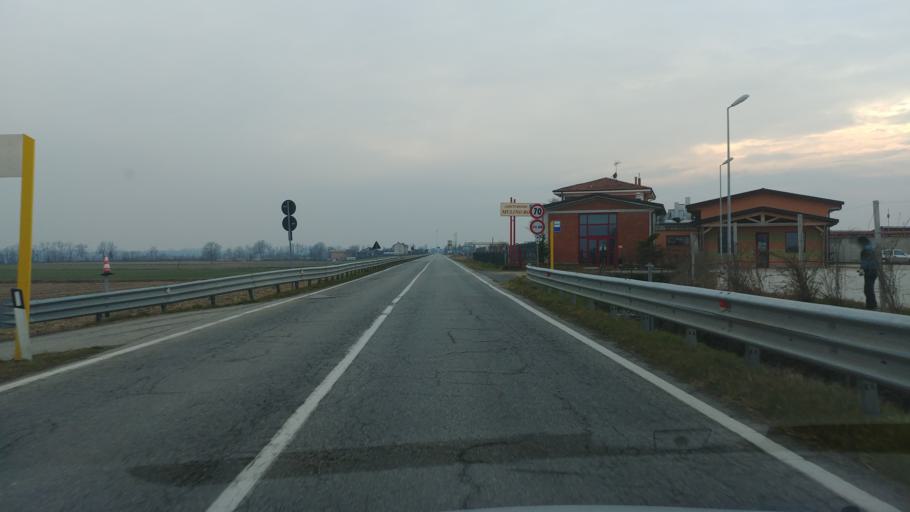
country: IT
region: Piedmont
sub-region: Provincia di Cuneo
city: Castelletto Stura
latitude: 44.4668
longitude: 7.6342
